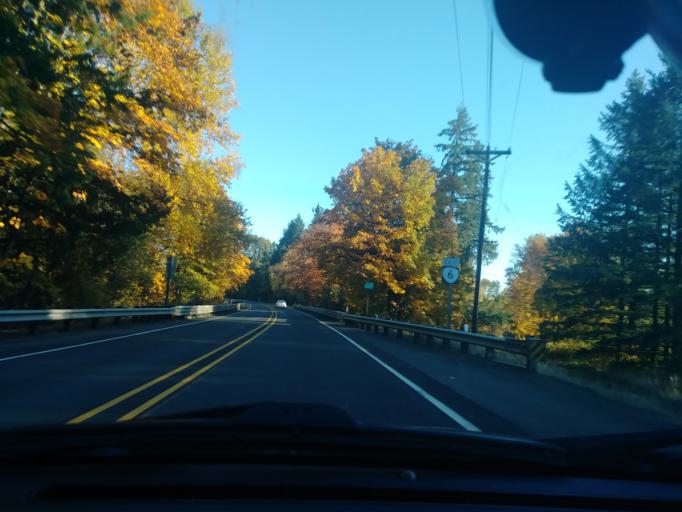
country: US
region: Oregon
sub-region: Washington County
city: Banks
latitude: 45.6116
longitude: -123.2430
